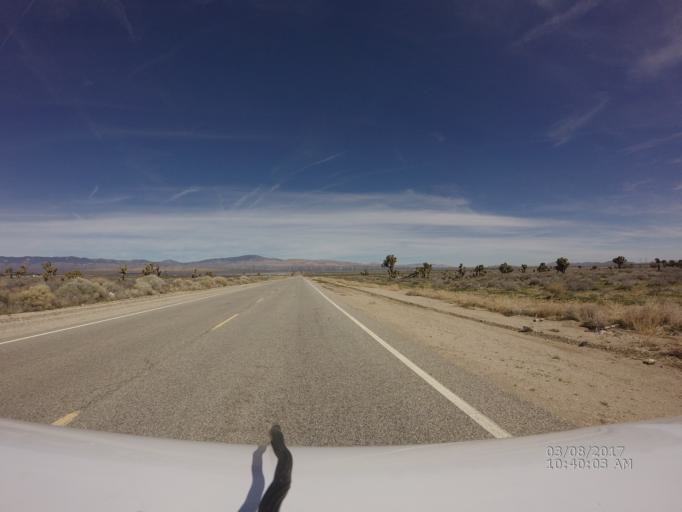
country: US
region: California
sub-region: Los Angeles County
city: Green Valley
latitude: 34.8015
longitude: -118.4315
